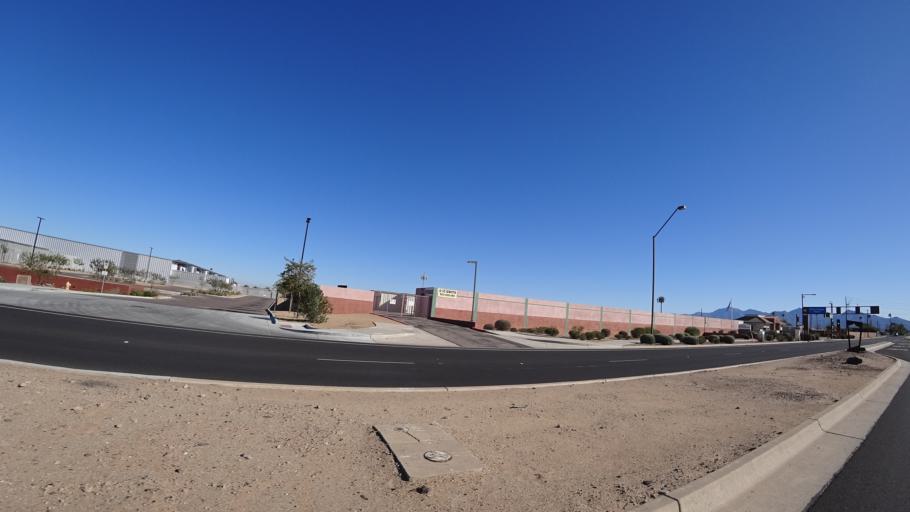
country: US
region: Arizona
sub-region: Maricopa County
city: Goodyear
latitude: 33.4283
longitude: -112.3581
